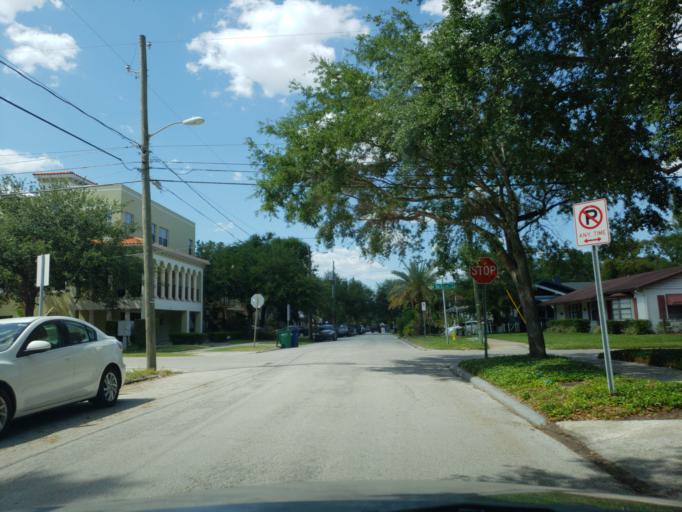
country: US
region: Florida
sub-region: Hillsborough County
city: Tampa
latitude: 27.9384
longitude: -82.4799
